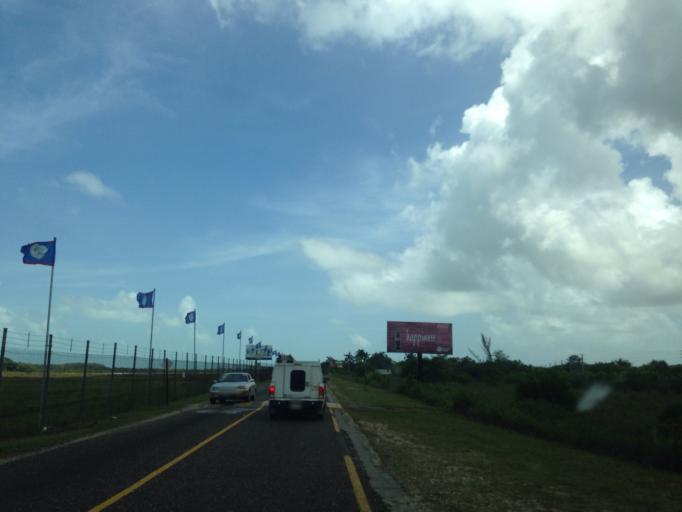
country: BZ
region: Belize
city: Belize City
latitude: 17.5376
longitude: -88.3048
